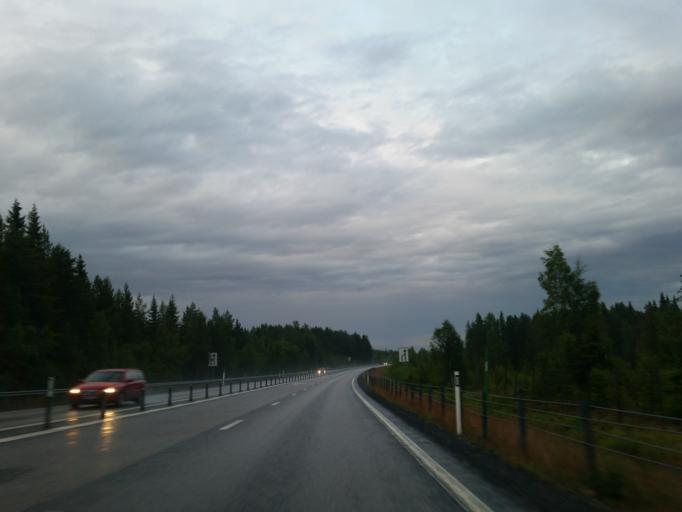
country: SE
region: Vaesterbotten
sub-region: Umea Kommun
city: Saevar
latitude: 63.9872
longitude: 20.7407
